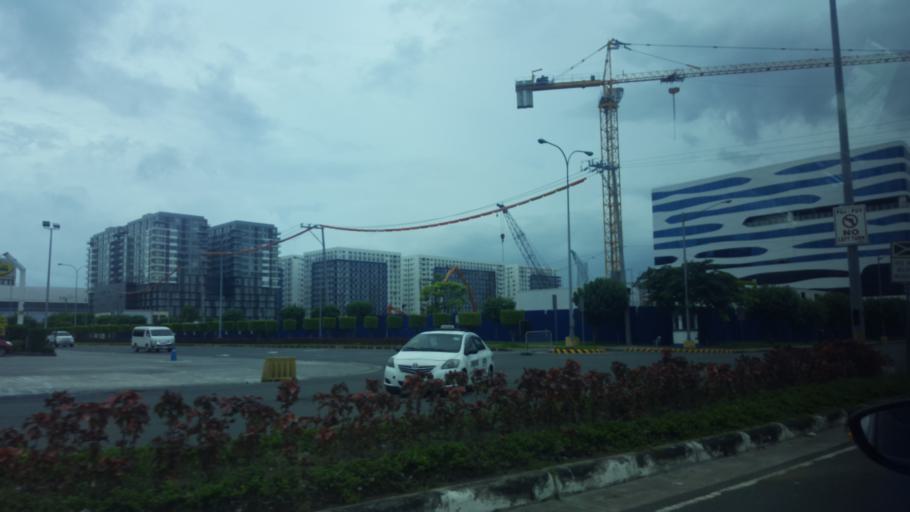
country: PH
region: Metro Manila
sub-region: Makati City
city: Makati City
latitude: 14.5316
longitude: 120.9897
